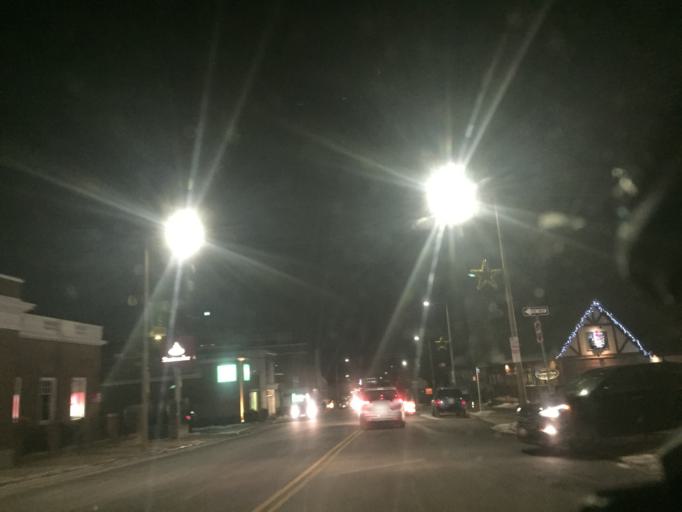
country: US
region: Massachusetts
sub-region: Middlesex County
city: Watertown
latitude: 42.3495
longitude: -71.1533
